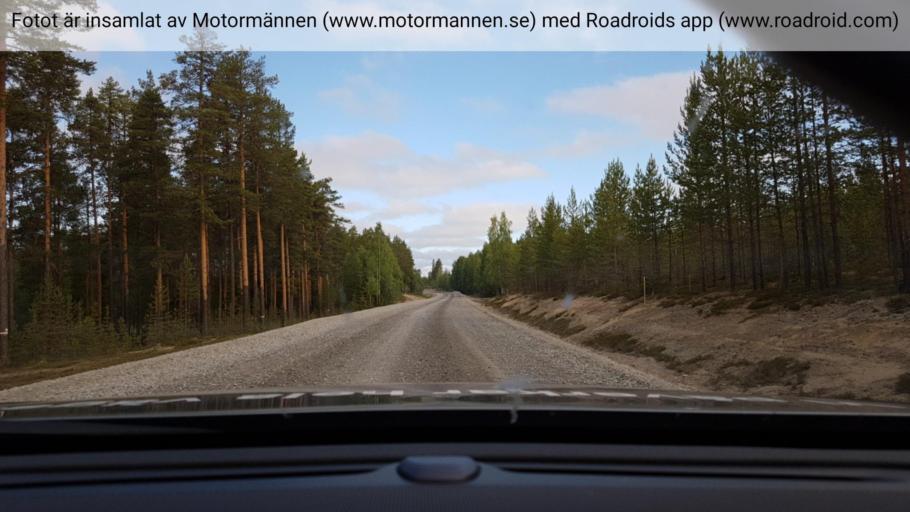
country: SE
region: Vaesterbotten
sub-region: Norsjo Kommun
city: Norsjoe
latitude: 64.6692
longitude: 19.2620
